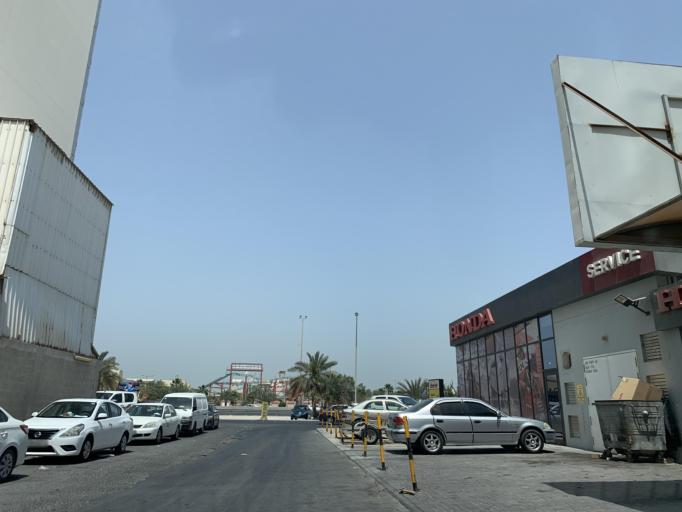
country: BH
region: Northern
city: Madinat `Isa
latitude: 26.1959
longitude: 50.5459
